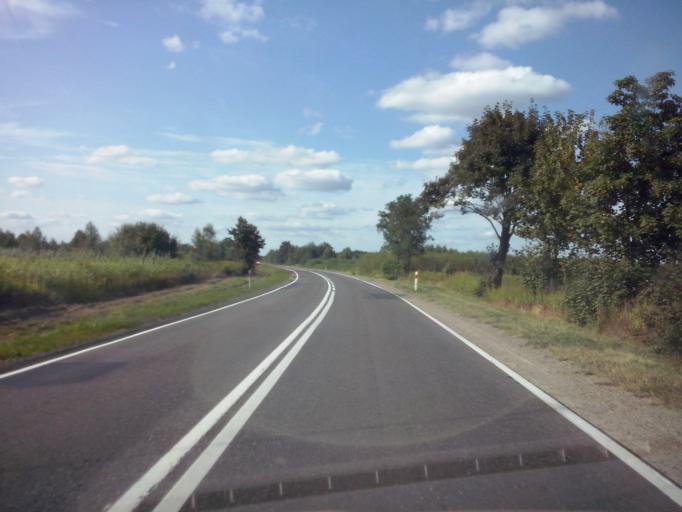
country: PL
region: Subcarpathian Voivodeship
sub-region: Powiat nizanski
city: Rudnik nad Sanem
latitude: 50.4669
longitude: 22.2420
